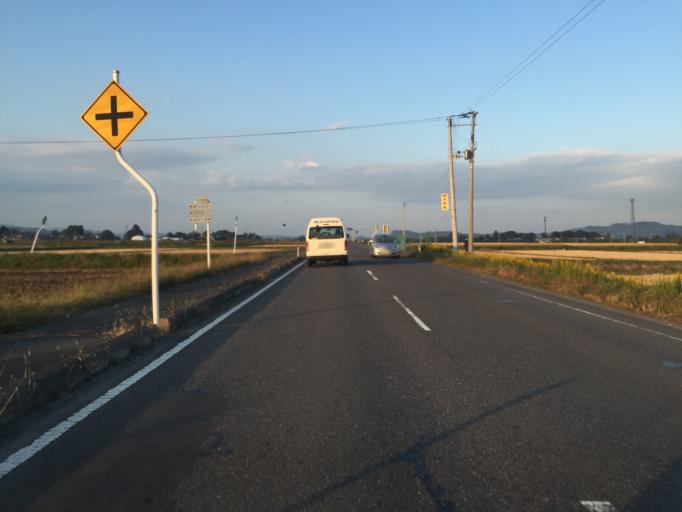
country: JP
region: Fukushima
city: Motomiya
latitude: 37.5284
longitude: 140.3771
